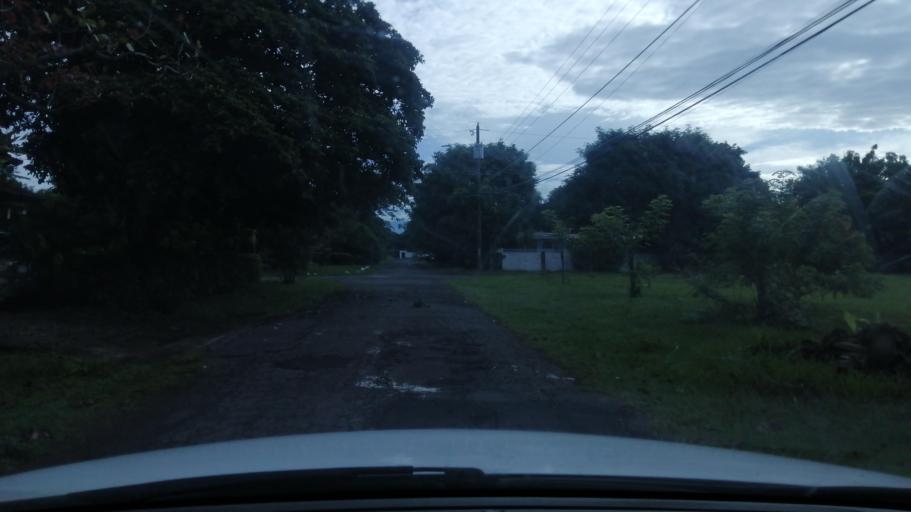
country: PA
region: Chiriqui
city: Mata del Nance
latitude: 8.4489
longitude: -82.4193
